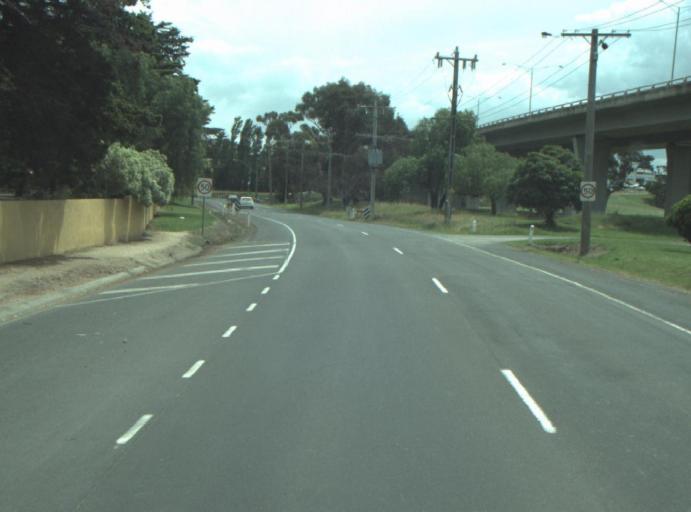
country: AU
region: Victoria
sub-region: Greater Geelong
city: Breakwater
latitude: -38.1667
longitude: 144.3504
